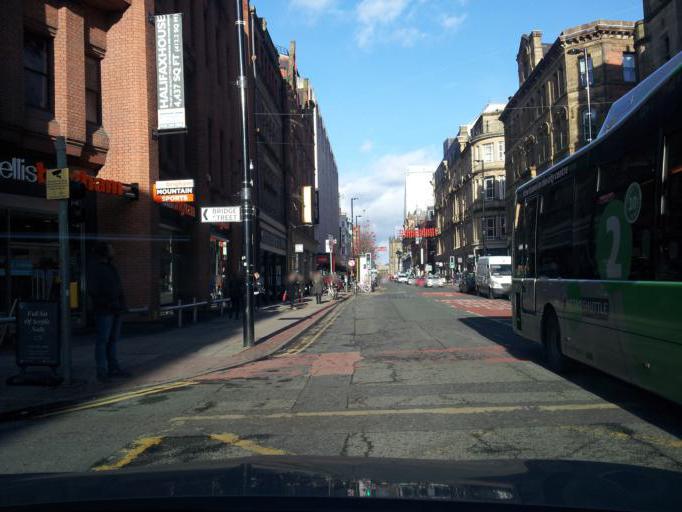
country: GB
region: England
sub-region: Manchester
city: Manchester
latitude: 53.4809
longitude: -2.2480
